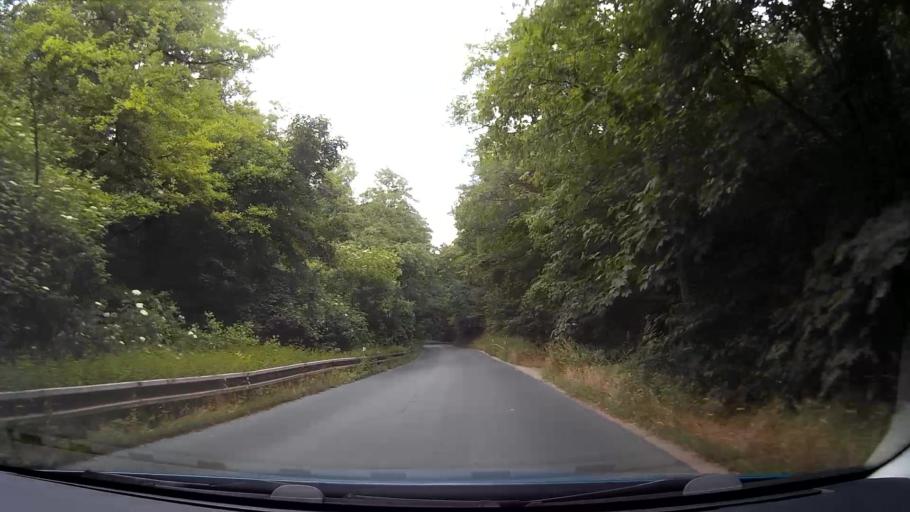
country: CZ
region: South Moravian
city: Orechov
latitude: 49.1253
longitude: 16.5270
